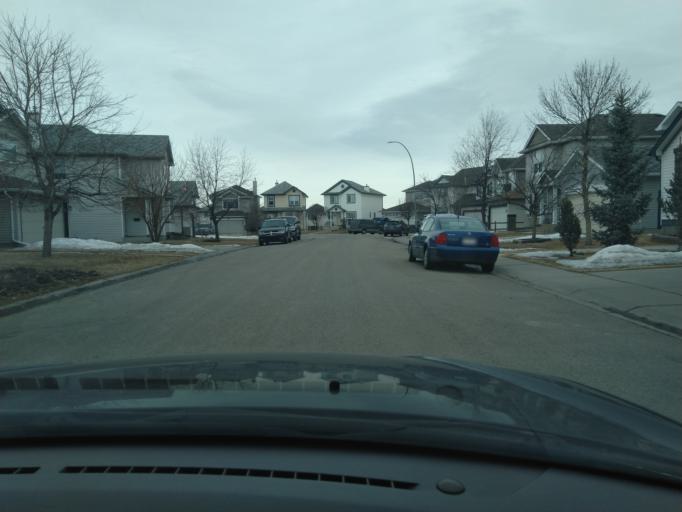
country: CA
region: Alberta
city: Calgary
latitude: 51.1702
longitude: -114.0447
